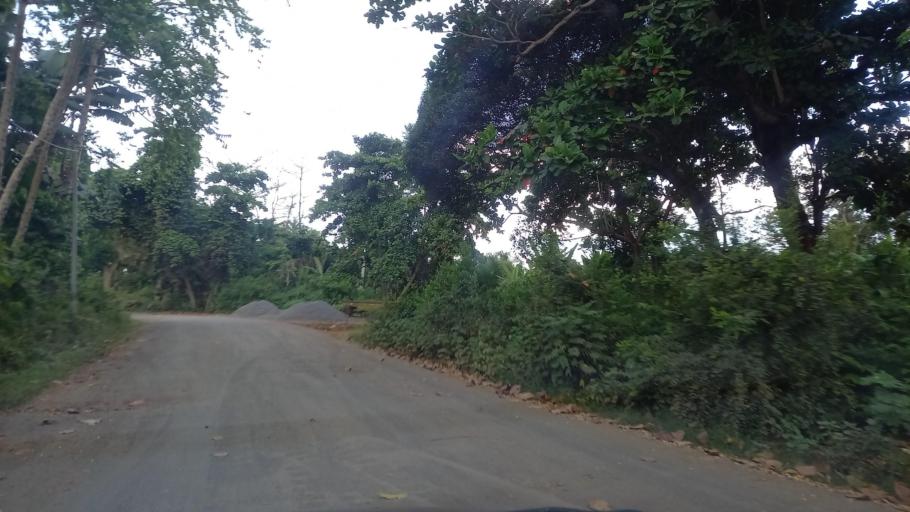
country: YT
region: Dembeni
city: Dembeni
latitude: -12.8298
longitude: 45.1911
